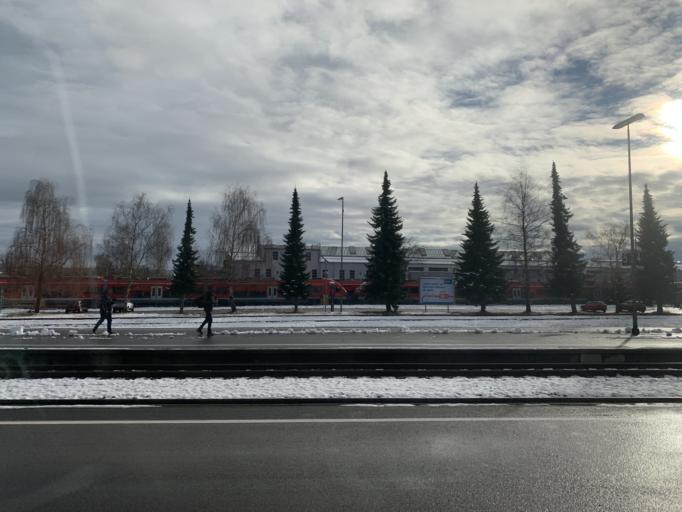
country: DE
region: Bavaria
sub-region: Swabia
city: Kempten (Allgaeu)
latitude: 47.7128
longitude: 10.3182
